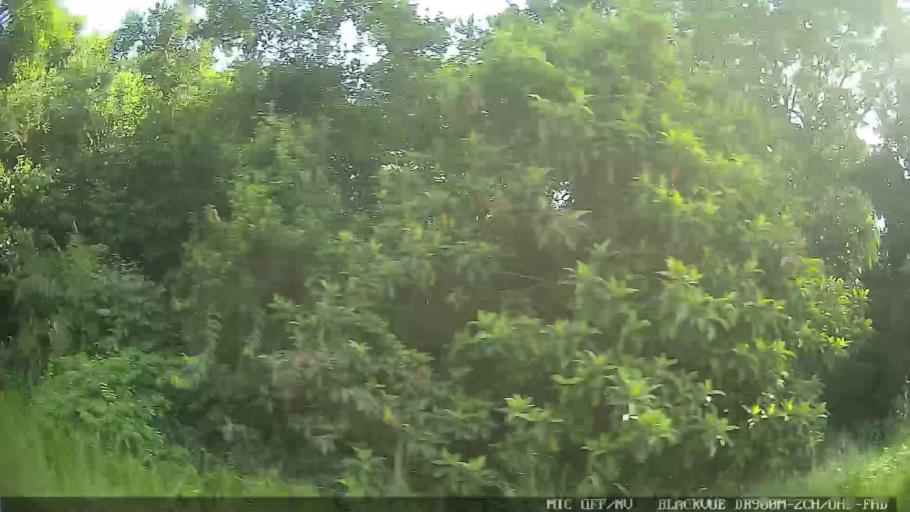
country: BR
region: Sao Paulo
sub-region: Bertioga
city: Bertioga
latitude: -23.8067
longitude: -46.0663
